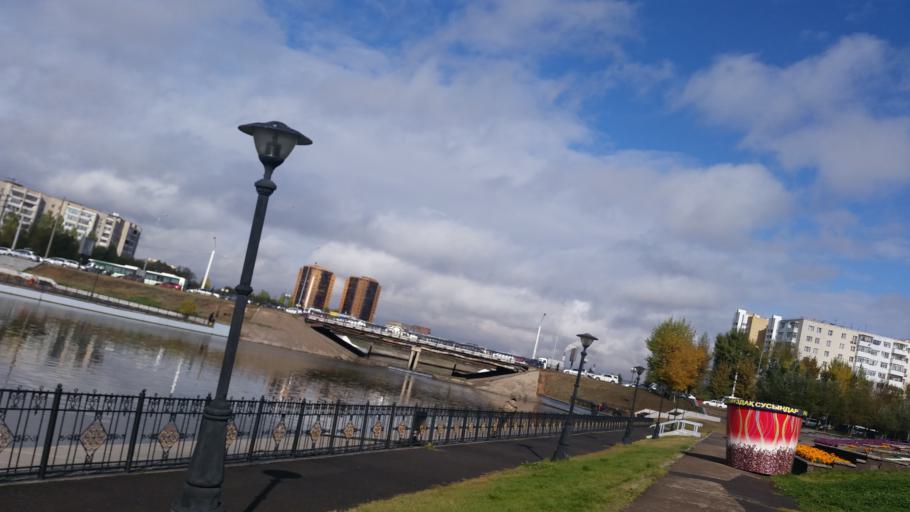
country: KZ
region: Astana Qalasy
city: Astana
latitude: 51.1595
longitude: 71.4689
